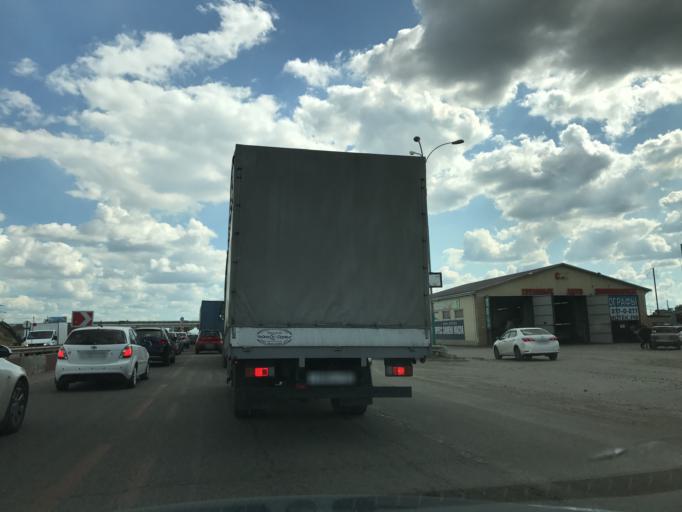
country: RU
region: Adygeya
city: Tlyustenkhabl'
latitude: 44.9526
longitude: 39.1229
